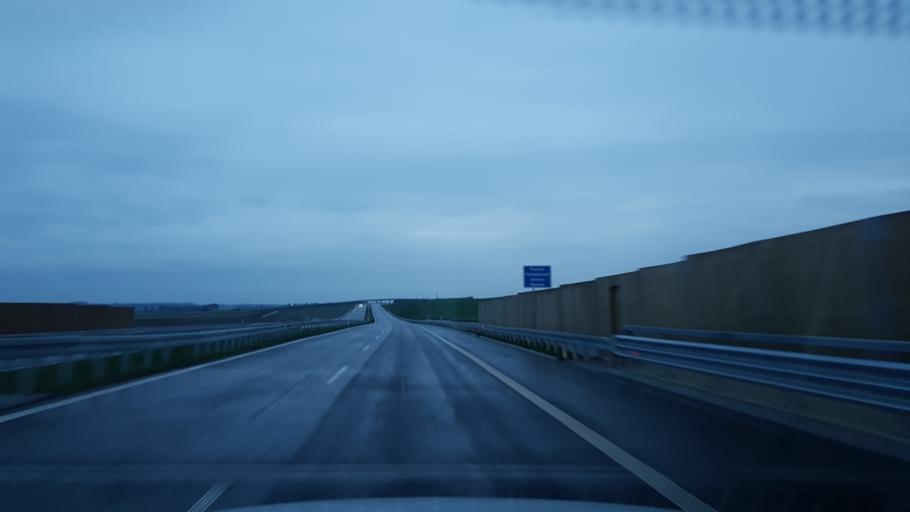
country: PL
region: West Pomeranian Voivodeship
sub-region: Powiat gryficki
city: Brojce
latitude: 53.9694
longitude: 15.4253
